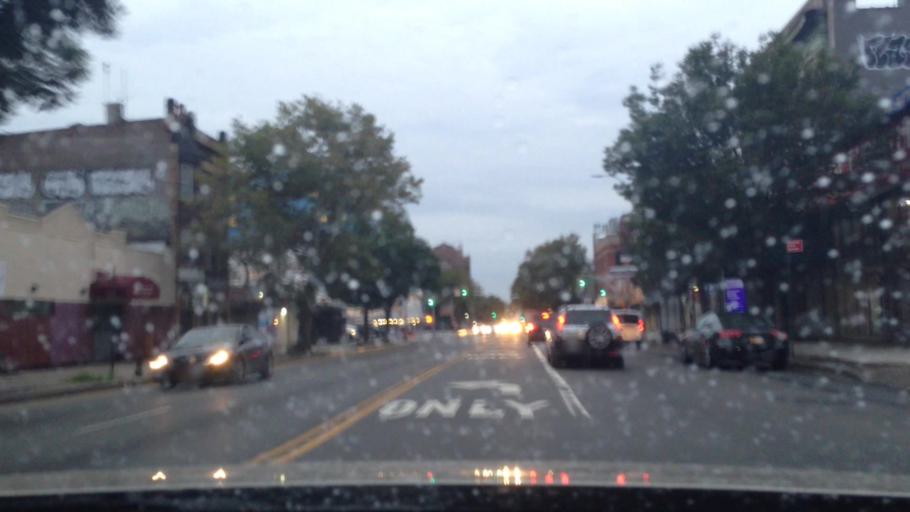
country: US
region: New York
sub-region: Kings County
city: East New York
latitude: 40.6768
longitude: -73.8972
